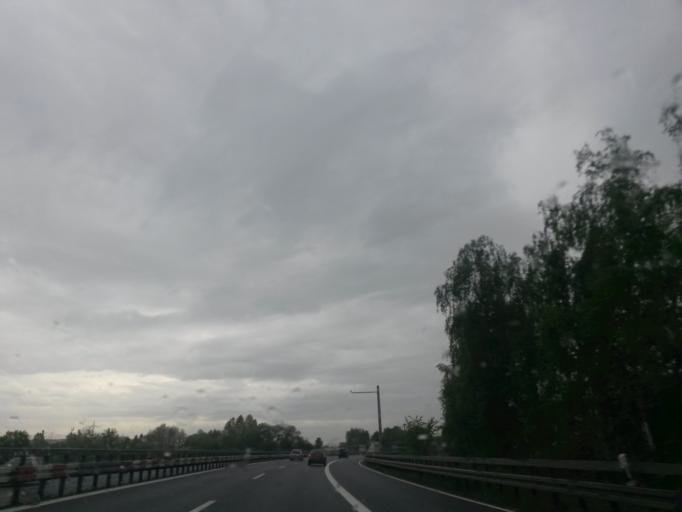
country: DE
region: Bavaria
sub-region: Regierungsbezirk Mittelfranken
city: Baiersdorf
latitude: 49.6537
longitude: 11.0335
